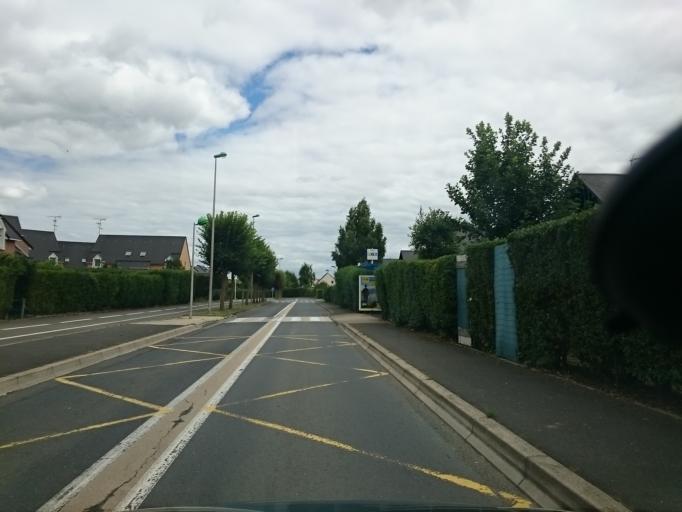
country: FR
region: Lower Normandy
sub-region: Departement du Calvados
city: Ifs
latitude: 49.1363
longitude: -0.3480
